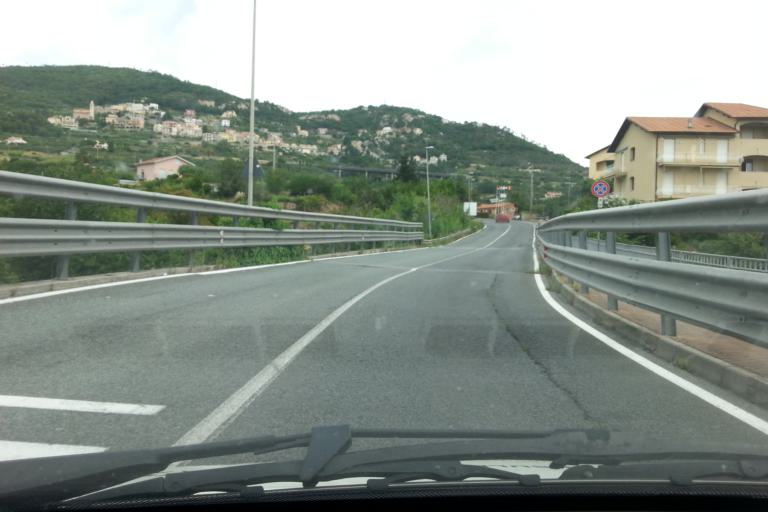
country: IT
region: Liguria
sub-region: Provincia di Savona
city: Pietra Ligure
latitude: 44.1474
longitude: 8.2689
